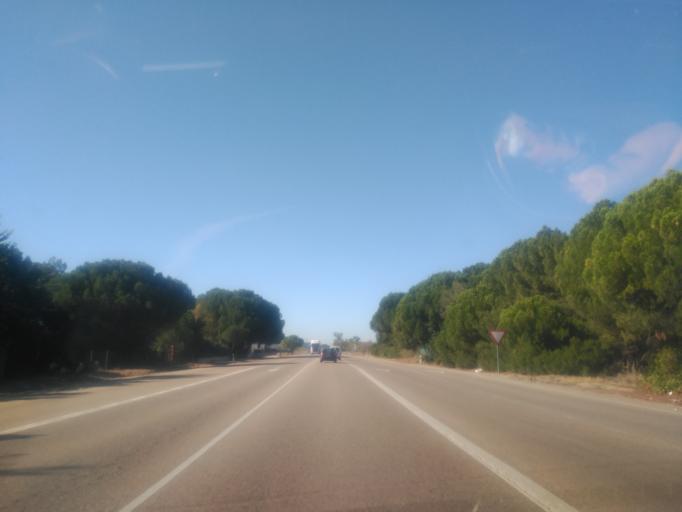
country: ES
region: Castille and Leon
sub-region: Provincia de Valladolid
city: Villabanez
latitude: 41.5945
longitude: -4.5189
